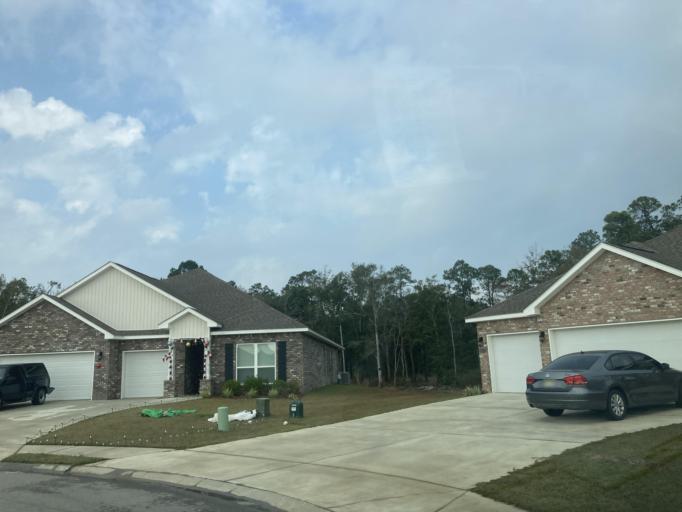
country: US
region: Mississippi
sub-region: Harrison County
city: Long Beach
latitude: 30.3762
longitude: -89.1609
